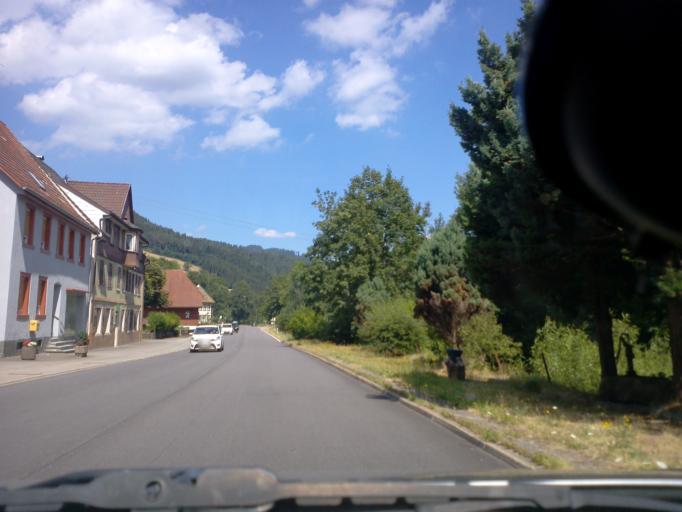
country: DE
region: Baden-Wuerttemberg
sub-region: Freiburg Region
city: Gutach (Schwarzwaldbahn)
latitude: 48.2286
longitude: 8.2196
